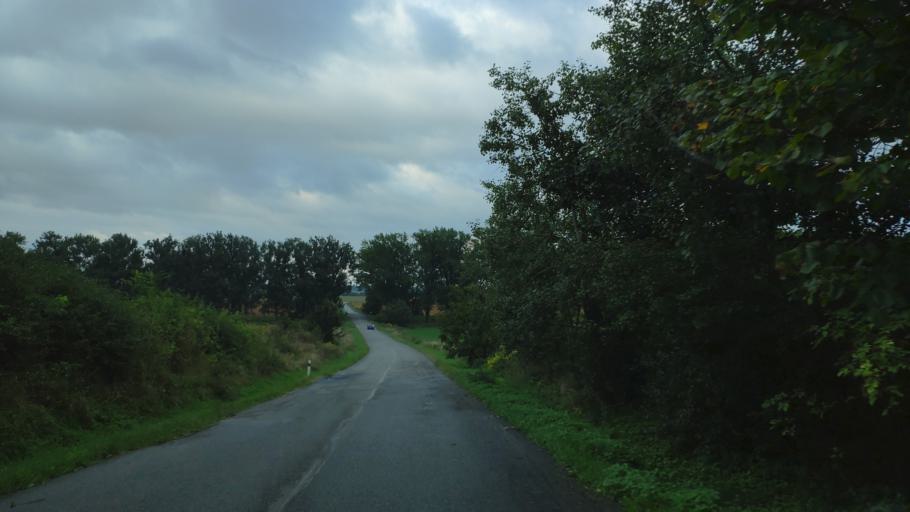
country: SK
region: Kosicky
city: Moldava nad Bodvou
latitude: 48.5824
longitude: 20.9317
